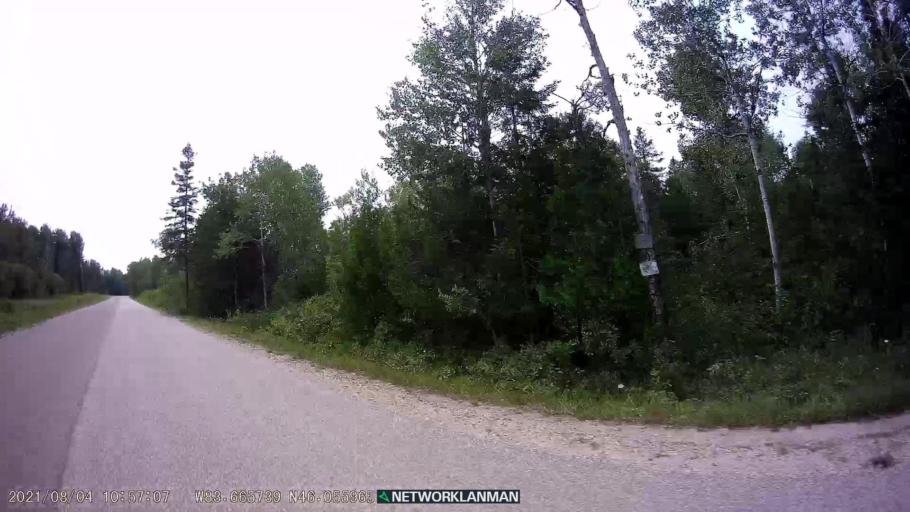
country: CA
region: Ontario
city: Thessalon
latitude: 46.0546
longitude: -83.6656
